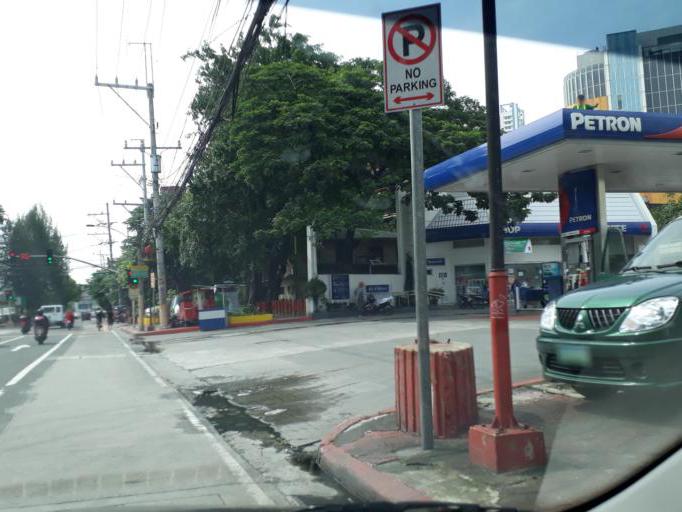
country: PH
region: Metro Manila
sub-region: City of Manila
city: Manila
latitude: 14.6156
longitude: 120.9872
